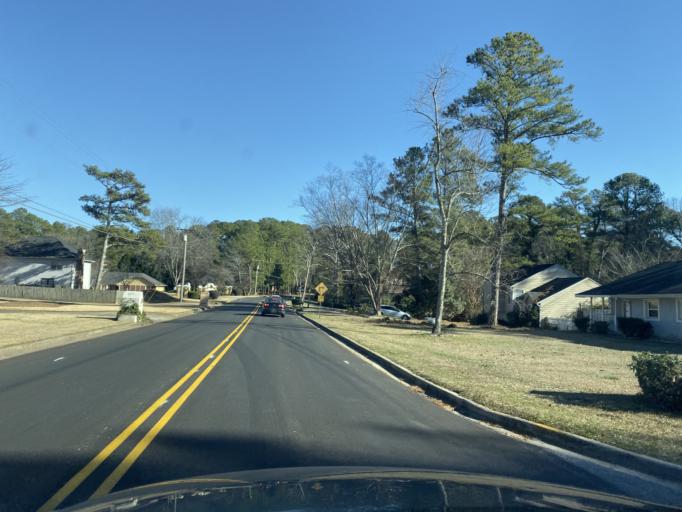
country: US
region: Georgia
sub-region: DeKalb County
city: Pine Mountain
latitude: 33.6757
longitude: -84.1588
